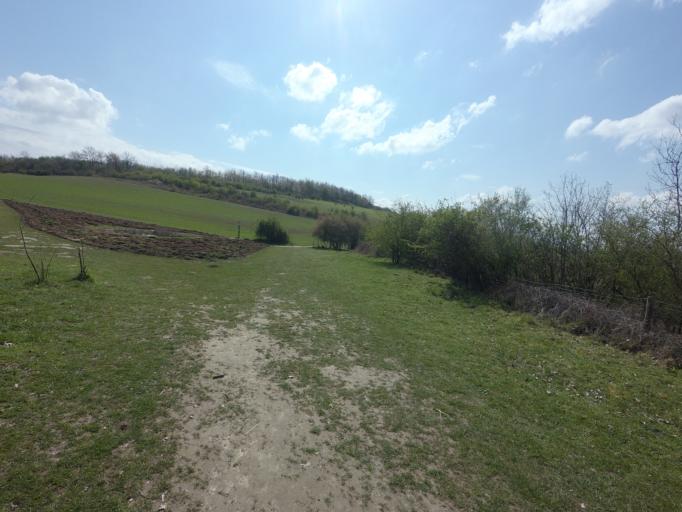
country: NL
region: Limburg
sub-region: Gemeente Maastricht
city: Maastricht
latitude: 50.8177
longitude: 5.6782
